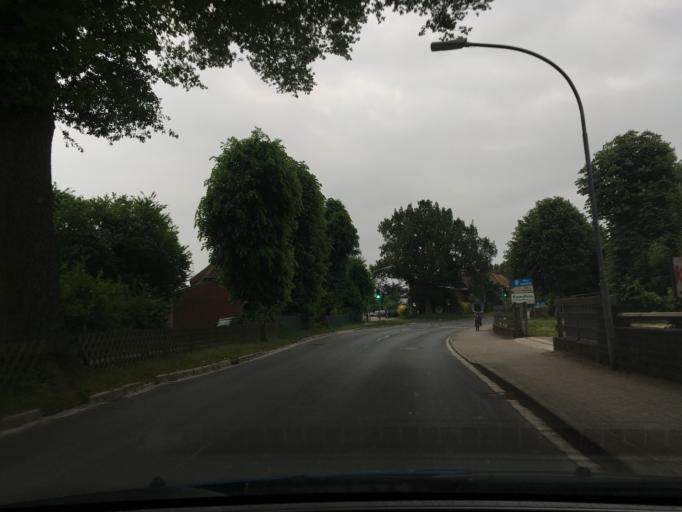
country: DE
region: Lower Saxony
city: Wulfsen
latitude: 53.3439
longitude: 10.1481
